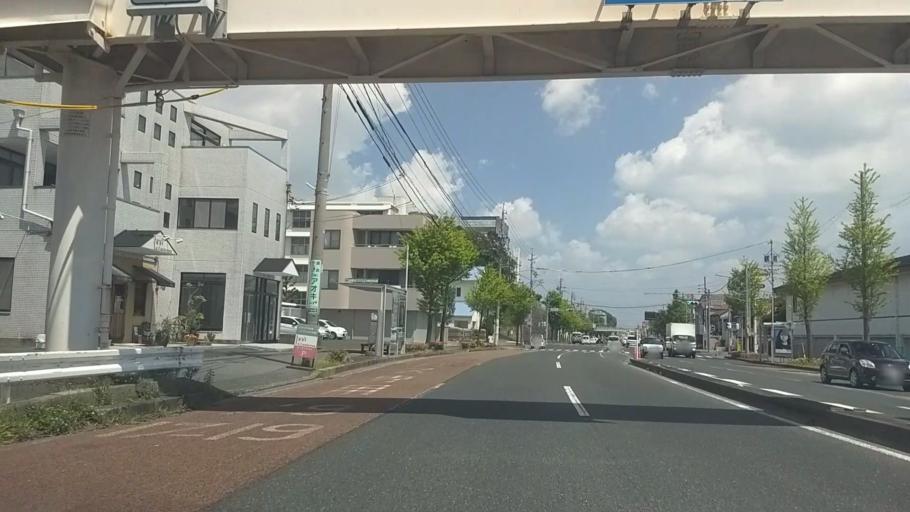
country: JP
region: Shizuoka
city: Hamamatsu
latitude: 34.7176
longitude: 137.7286
